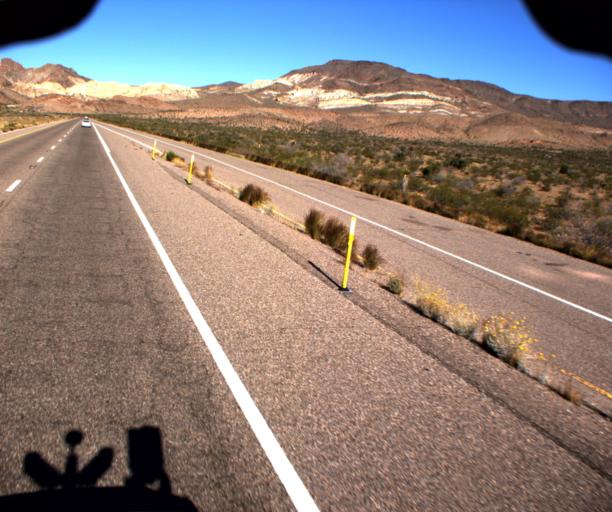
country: US
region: Arizona
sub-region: Mohave County
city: Golden Valley
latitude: 35.2290
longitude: -114.3602
